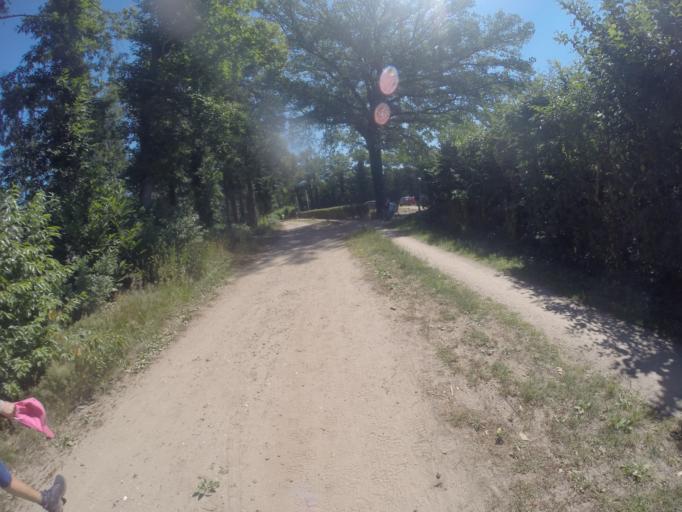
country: NL
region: Gelderland
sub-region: Gemeente Lochem
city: Barchem
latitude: 52.1276
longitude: 6.4356
